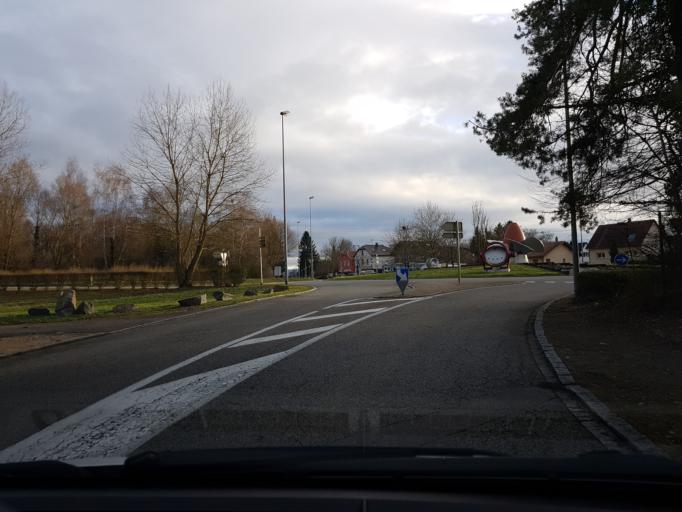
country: FR
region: Alsace
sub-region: Departement du Haut-Rhin
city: Kembs
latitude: 47.6599
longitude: 7.5135
